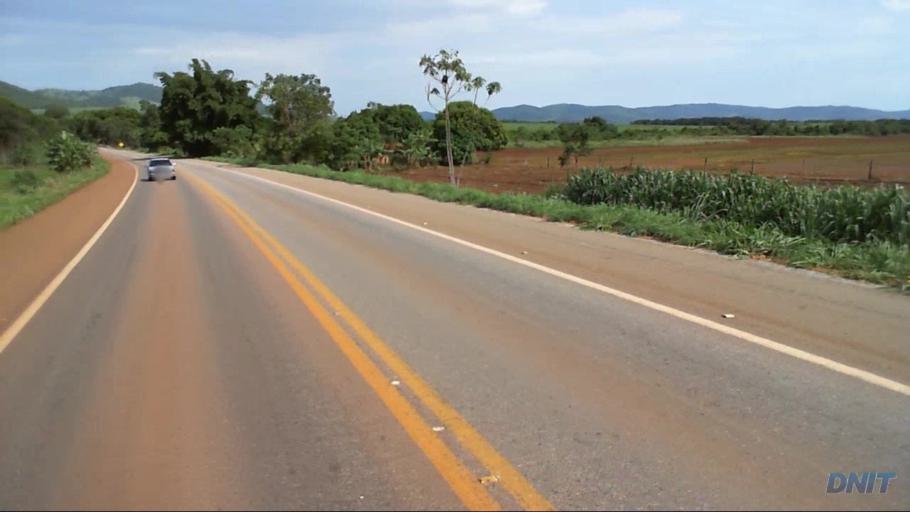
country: BR
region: Goias
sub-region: Barro Alto
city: Barro Alto
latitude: -15.0552
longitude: -48.8811
